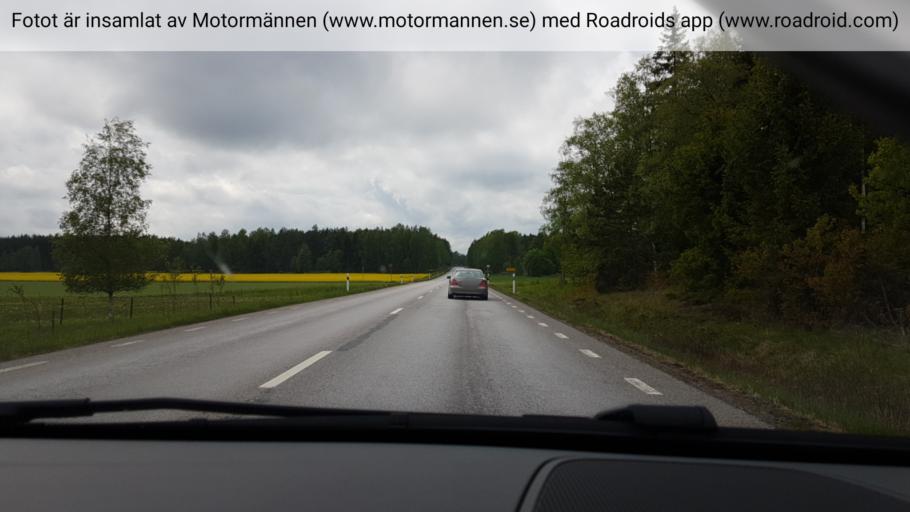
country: SE
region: Uppsala
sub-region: Osthammars Kommun
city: Osterbybruk
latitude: 60.1615
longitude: 18.0116
